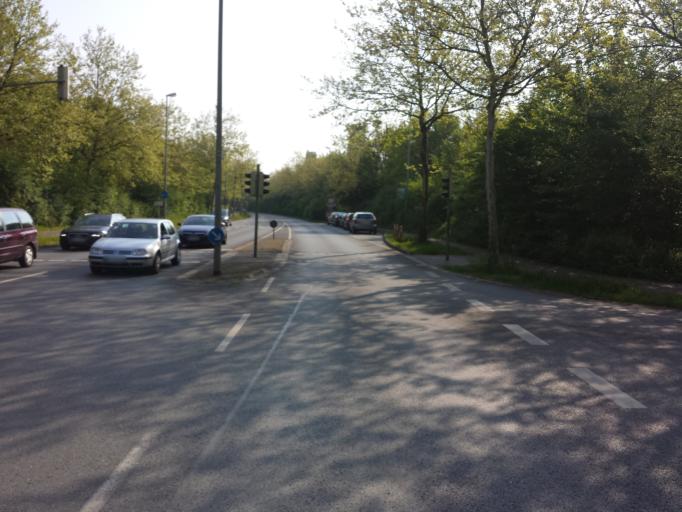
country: DE
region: North Rhine-Westphalia
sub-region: Regierungsbezirk Detmold
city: Guetersloh
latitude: 51.8841
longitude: 8.3826
